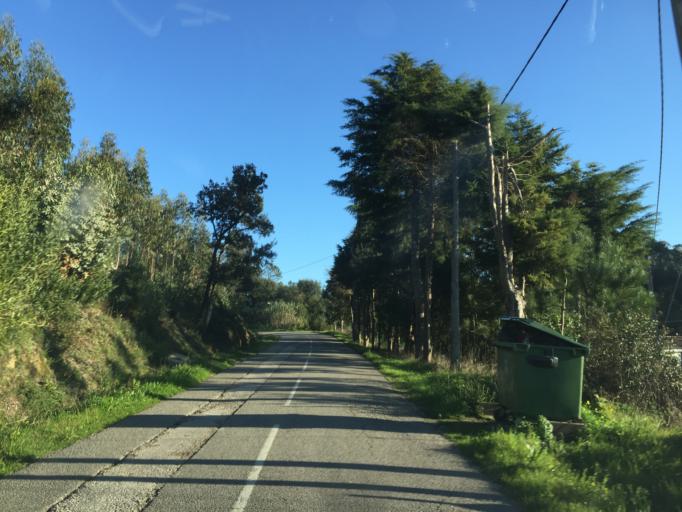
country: PT
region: Coimbra
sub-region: Figueira da Foz
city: Alhadas
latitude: 40.1629
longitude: -8.8086
